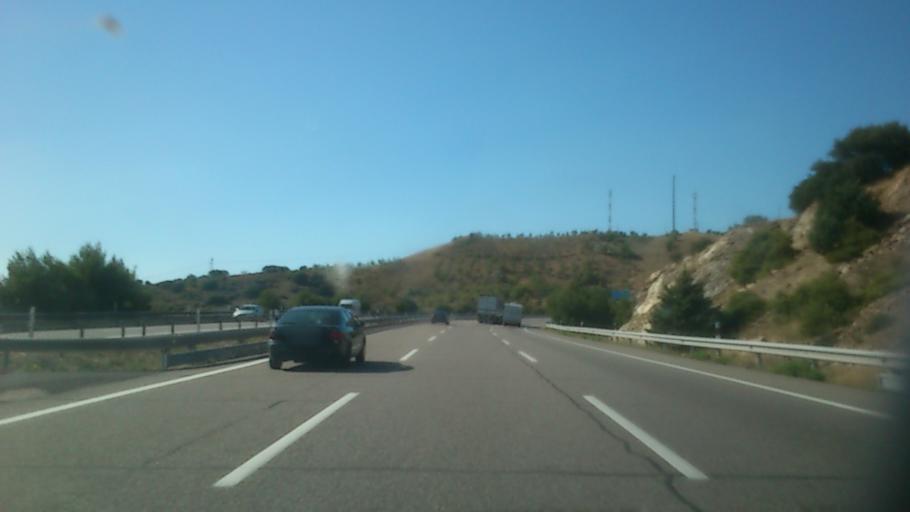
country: ES
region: Aragon
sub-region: Provincia de Zaragoza
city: Paracuellos de la Ribera
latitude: 41.4075
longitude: -1.5260
